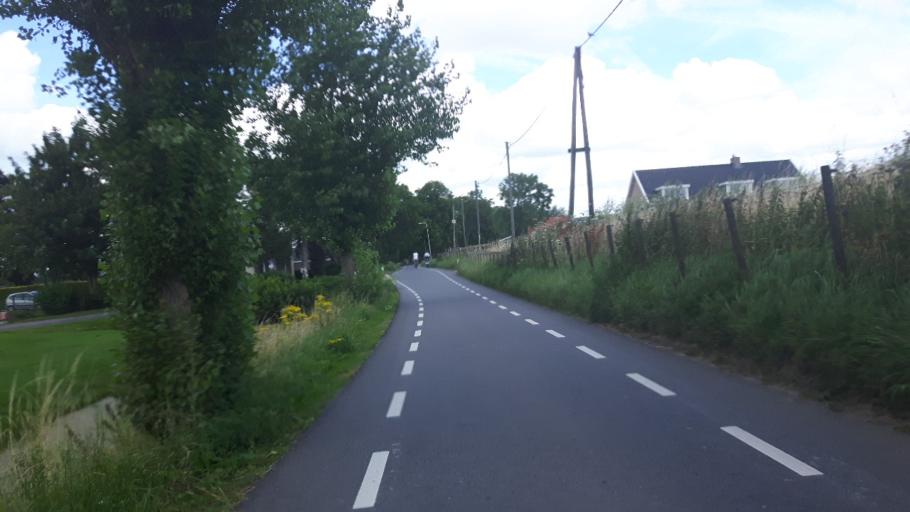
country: NL
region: Utrecht
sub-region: Gemeente Oudewater
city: Oudewater
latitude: 52.0216
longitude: 4.8566
